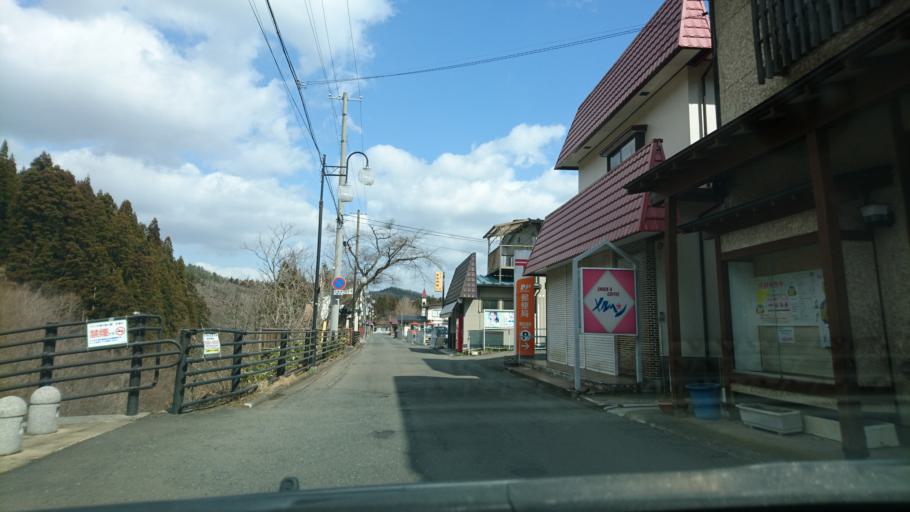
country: JP
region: Iwate
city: Shizukuishi
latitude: 39.6368
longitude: 140.9234
